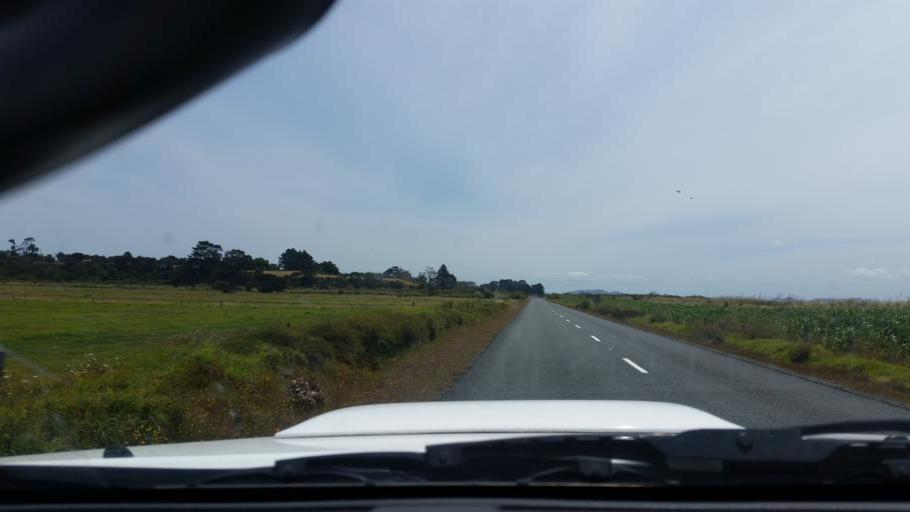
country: NZ
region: Northland
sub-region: Kaipara District
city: Dargaville
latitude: -36.1801
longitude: 174.0303
